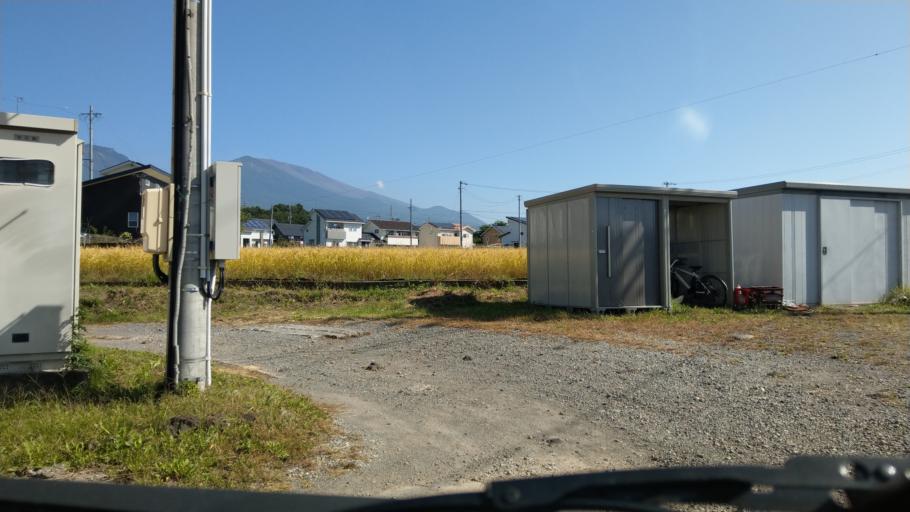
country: JP
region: Nagano
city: Komoro
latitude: 36.3218
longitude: 138.4448
